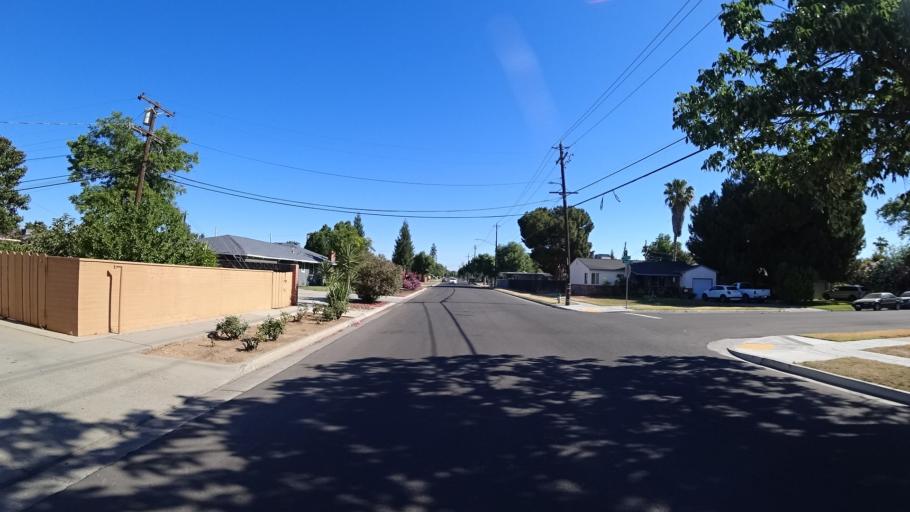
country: US
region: California
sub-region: Fresno County
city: Fresno
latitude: 36.7828
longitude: -119.8310
